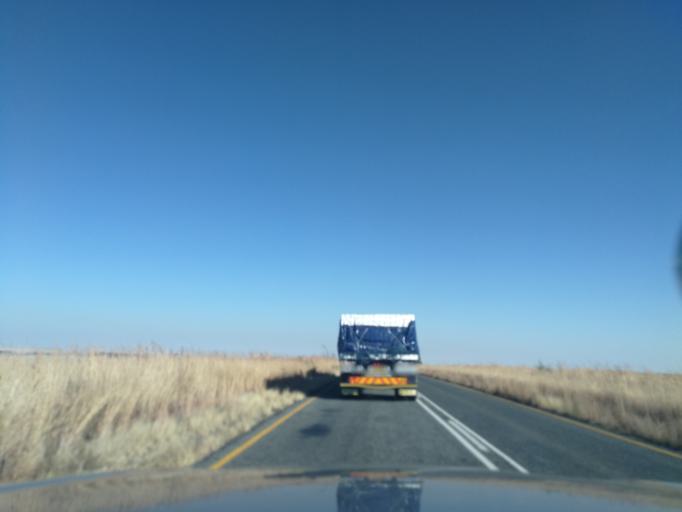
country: ZA
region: Orange Free State
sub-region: Thabo Mofutsanyana District Municipality
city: Senekal
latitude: -27.9523
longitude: 27.5978
